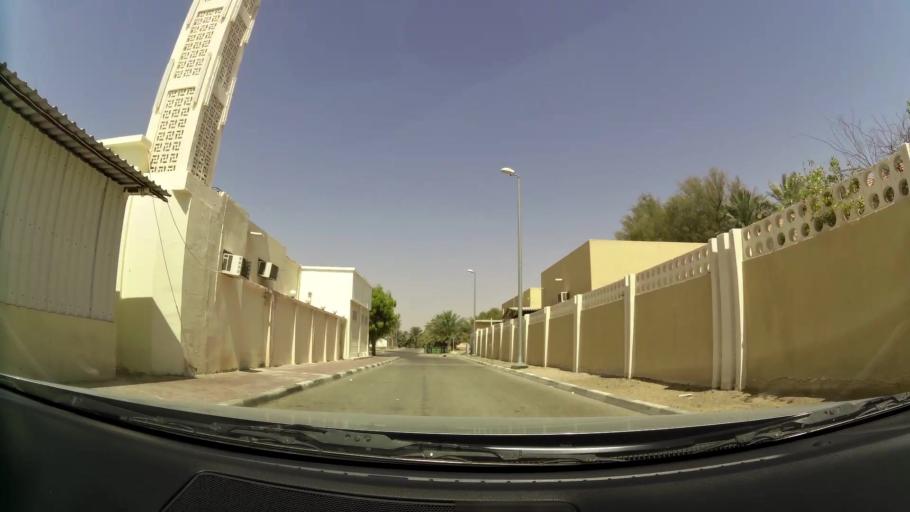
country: OM
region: Al Buraimi
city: Al Buraymi
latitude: 24.2905
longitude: 55.7667
